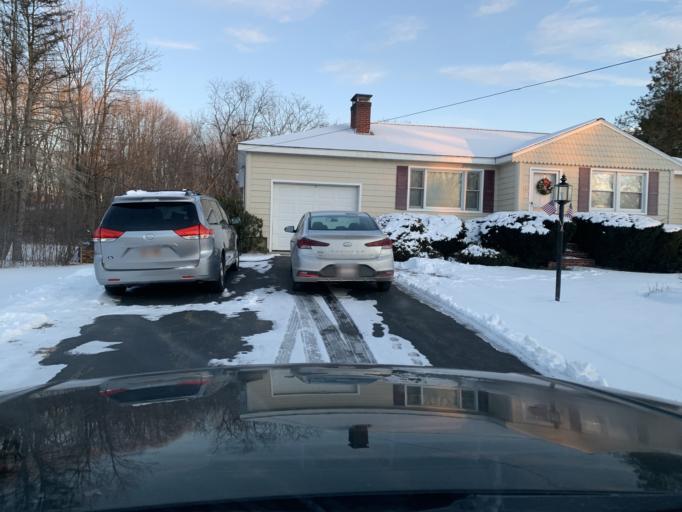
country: US
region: Massachusetts
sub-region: Essex County
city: Haverhill
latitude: 42.7803
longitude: -71.1116
